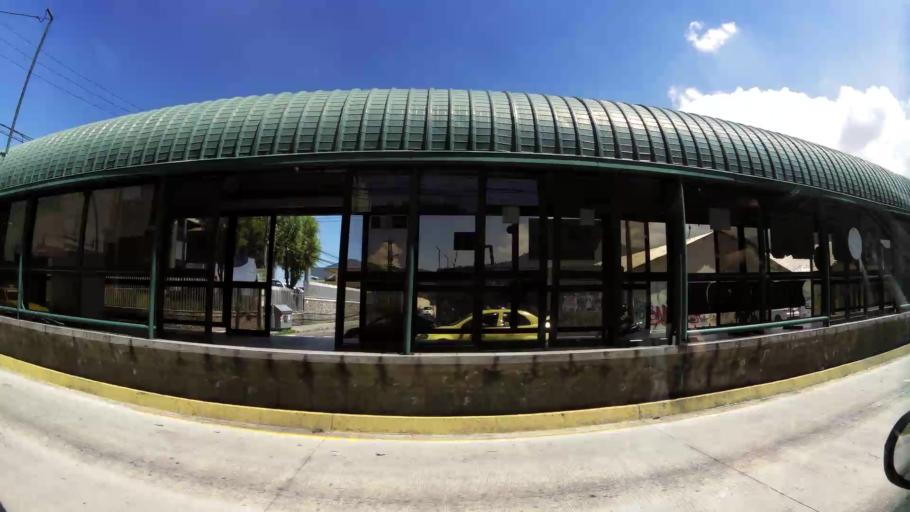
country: EC
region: Pichincha
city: Quito
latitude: -0.2599
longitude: -78.5228
